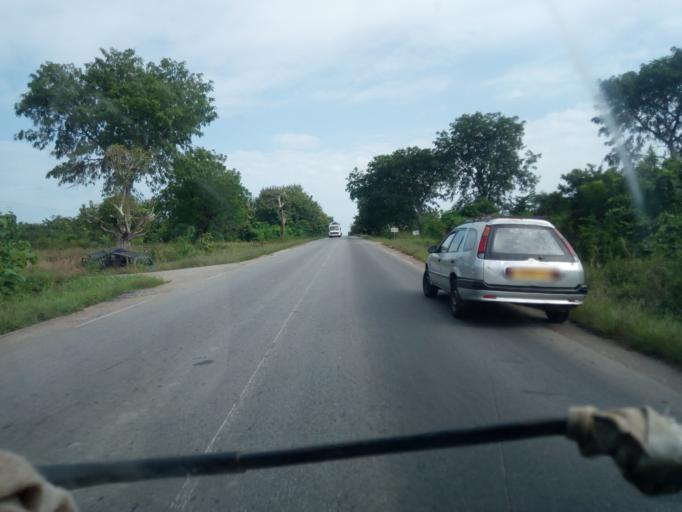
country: TG
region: Plateaux
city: Notse
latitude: 7.0033
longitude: 1.1655
